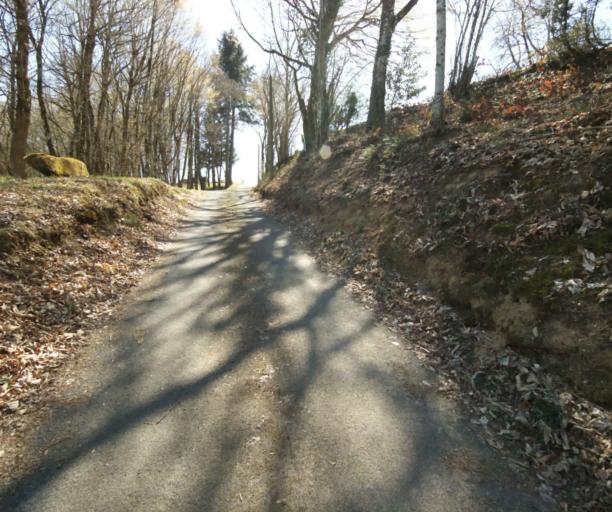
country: FR
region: Limousin
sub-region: Departement de la Correze
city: Saint-Clement
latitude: 45.3293
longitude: 1.6993
